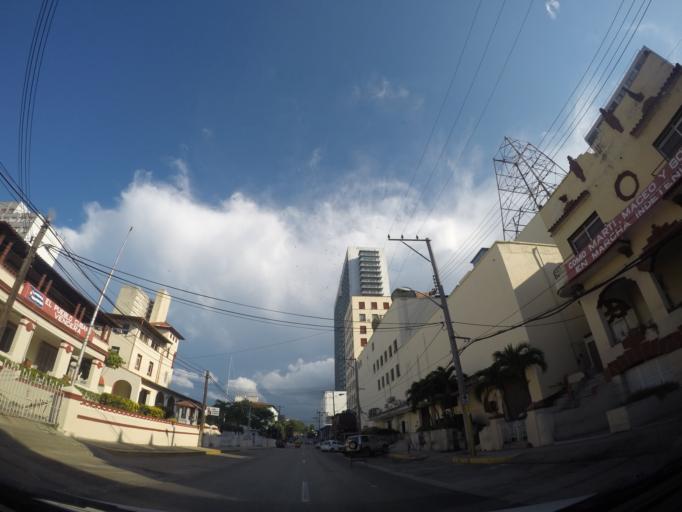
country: CU
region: La Habana
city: Havana
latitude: 23.1410
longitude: -82.3832
